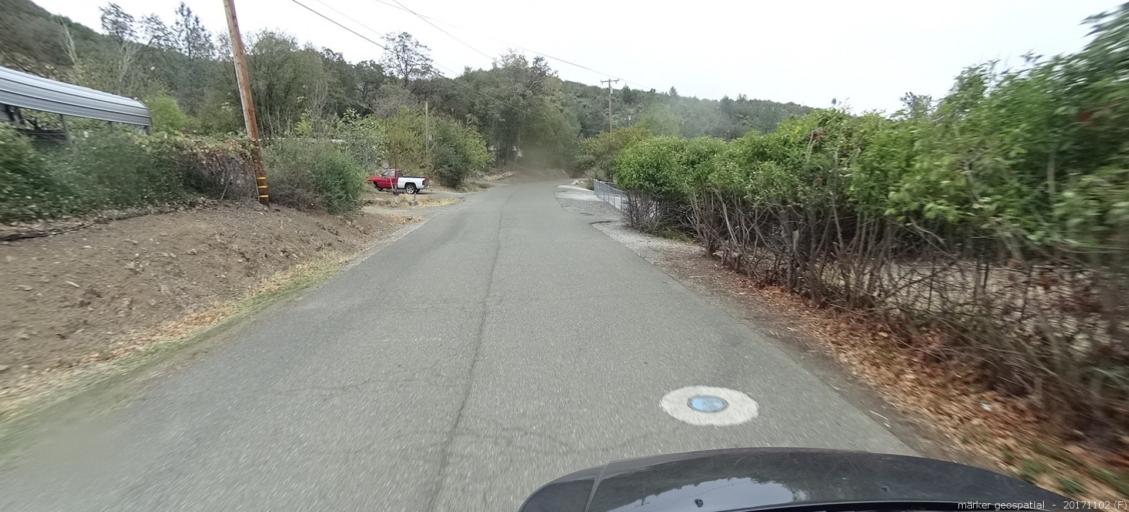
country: US
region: California
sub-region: Shasta County
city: Bella Vista
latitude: 40.7180
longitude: -122.2334
